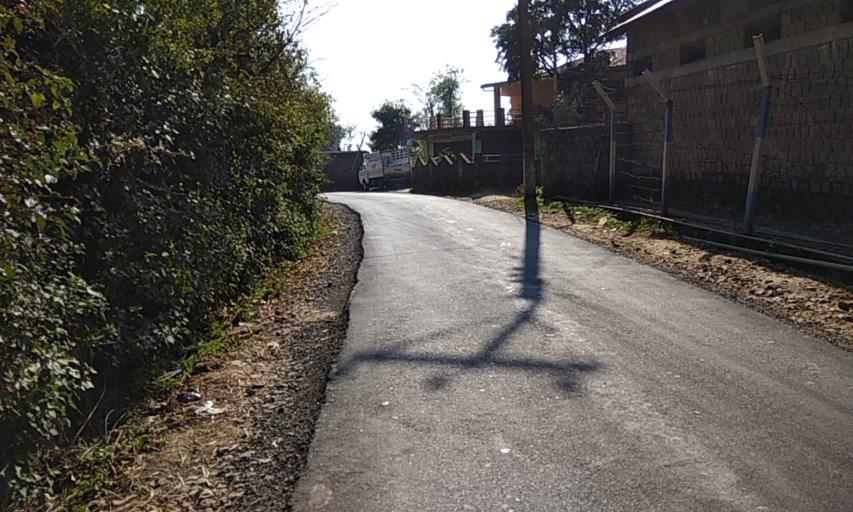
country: IN
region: Himachal Pradesh
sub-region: Kangra
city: Palampur
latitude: 32.1173
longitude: 76.5252
